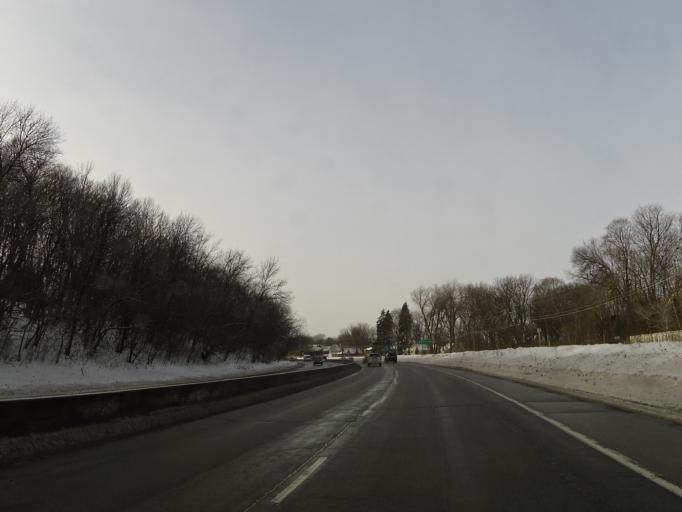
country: US
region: Minnesota
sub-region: Hennepin County
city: Excelsior
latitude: 44.9055
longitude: -93.5439
